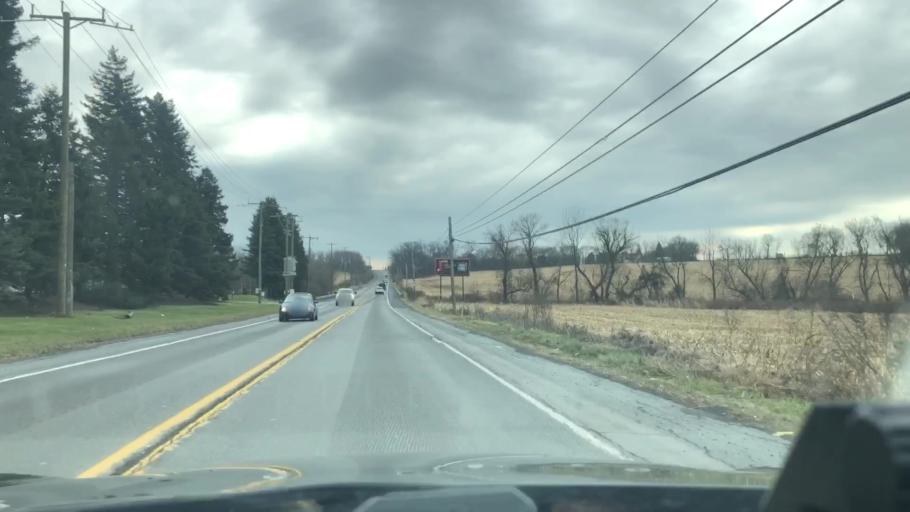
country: US
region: Pennsylvania
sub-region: Northampton County
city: Nazareth
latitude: 40.7287
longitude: -75.3026
